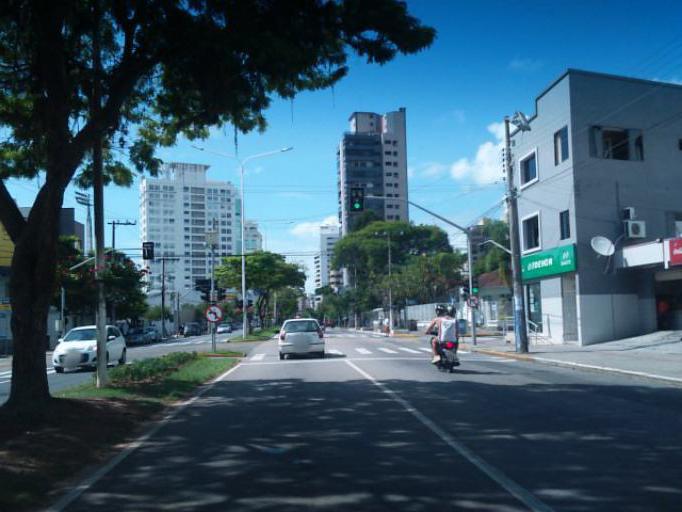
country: BR
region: Santa Catarina
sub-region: Itajai
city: Itajai
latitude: -26.9076
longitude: -48.6614
